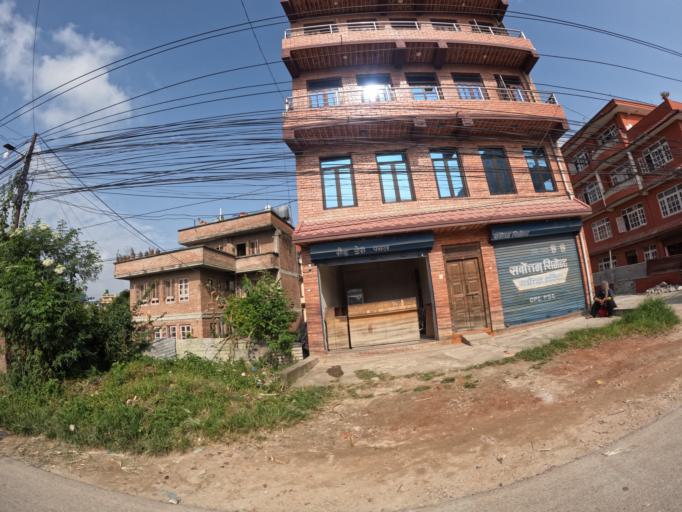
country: NP
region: Central Region
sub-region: Bagmati Zone
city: Bhaktapur
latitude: 27.6803
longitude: 85.4454
